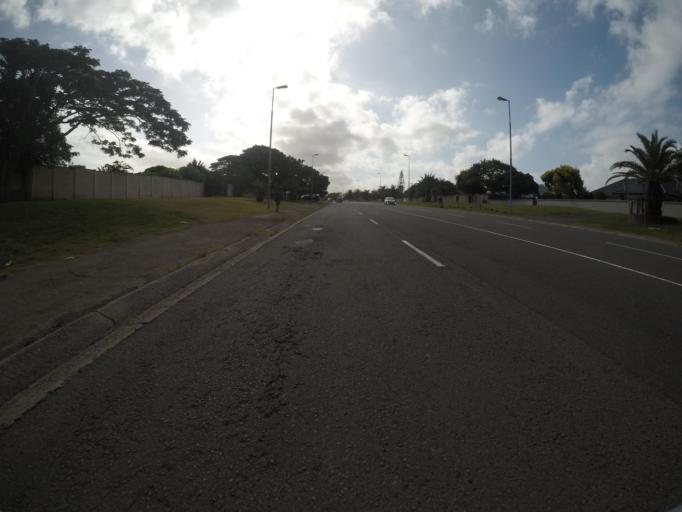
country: ZA
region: Eastern Cape
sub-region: Buffalo City Metropolitan Municipality
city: East London
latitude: -32.9668
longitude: 27.9447
